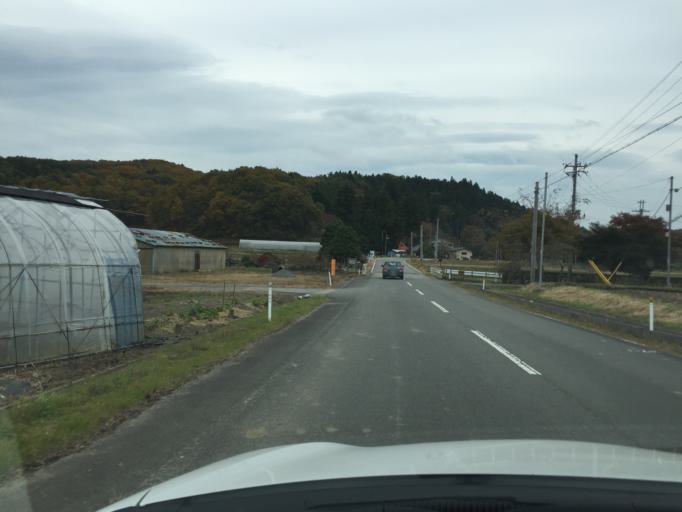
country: JP
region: Fukushima
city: Iwaki
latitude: 37.1801
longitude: 140.7194
